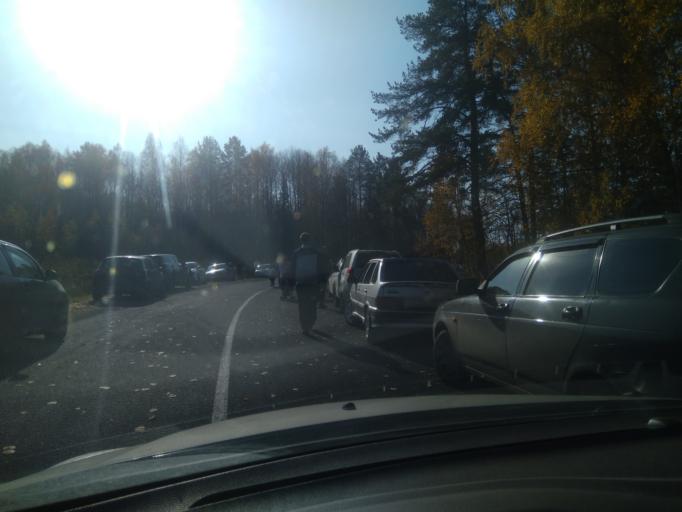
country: RU
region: Sverdlovsk
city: Mikhaylovsk
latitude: 56.5288
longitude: 59.2269
